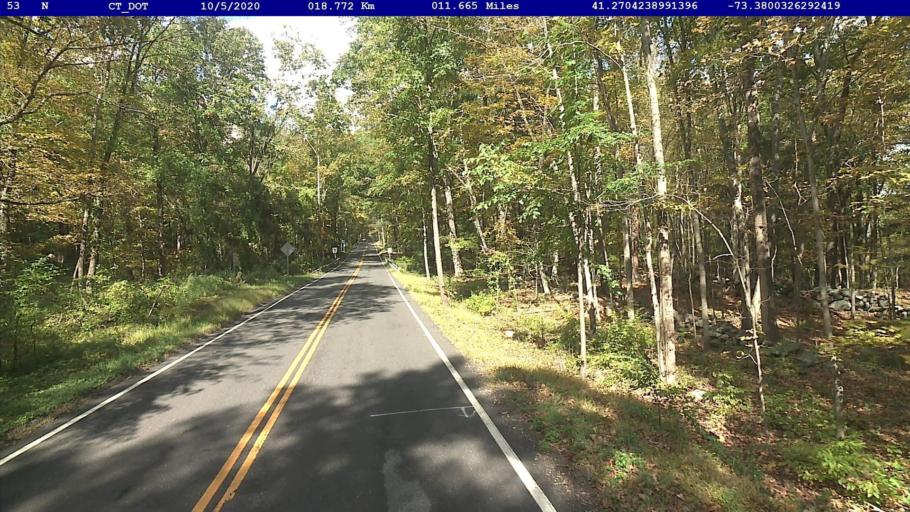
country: US
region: Connecticut
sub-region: Fairfield County
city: Georgetown
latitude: 41.2704
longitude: -73.3800
